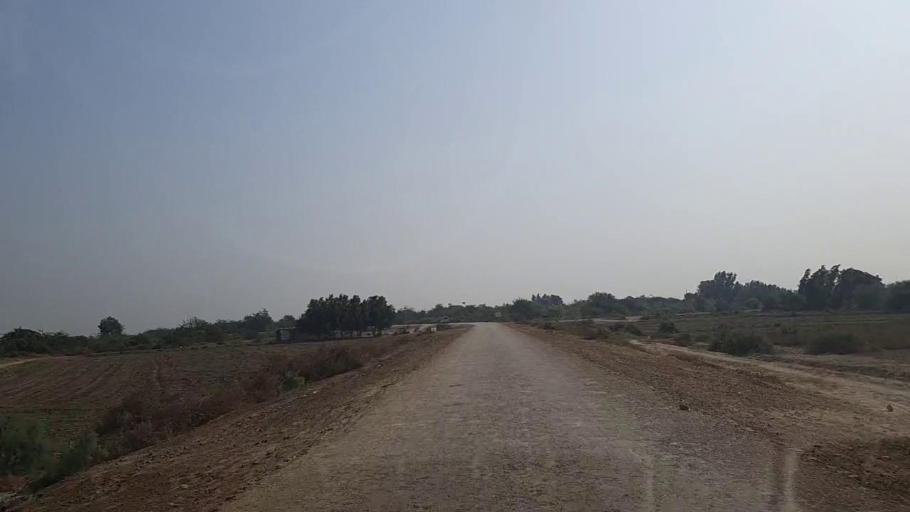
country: PK
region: Sindh
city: Keti Bandar
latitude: 24.2450
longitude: 67.7001
